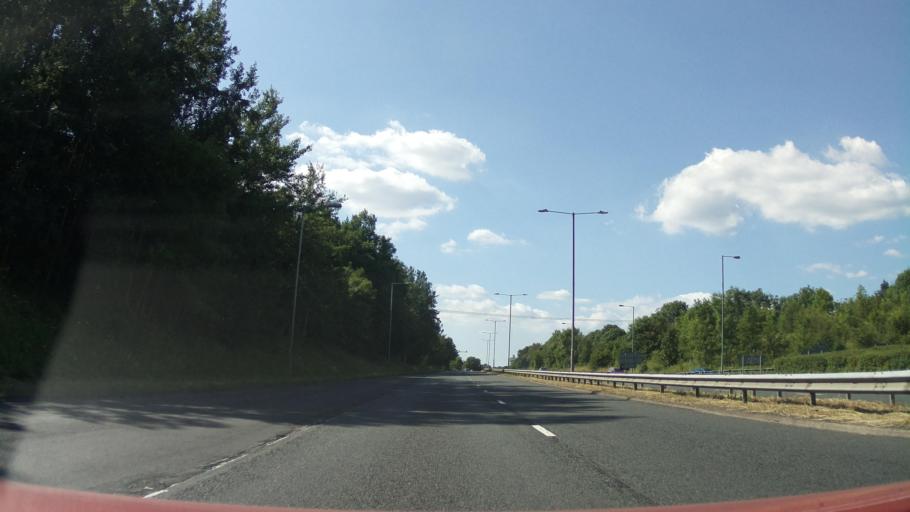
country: GB
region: England
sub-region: Worcestershire
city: Redditch
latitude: 52.3063
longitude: -1.9794
